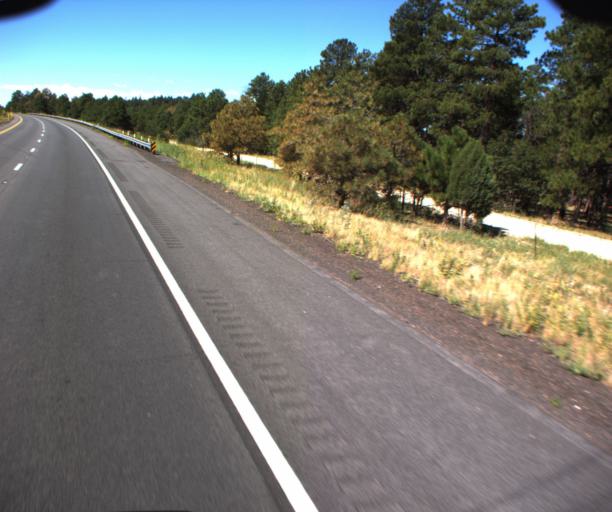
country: US
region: Arizona
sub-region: Coconino County
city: Williams
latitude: 35.2323
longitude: -112.2325
